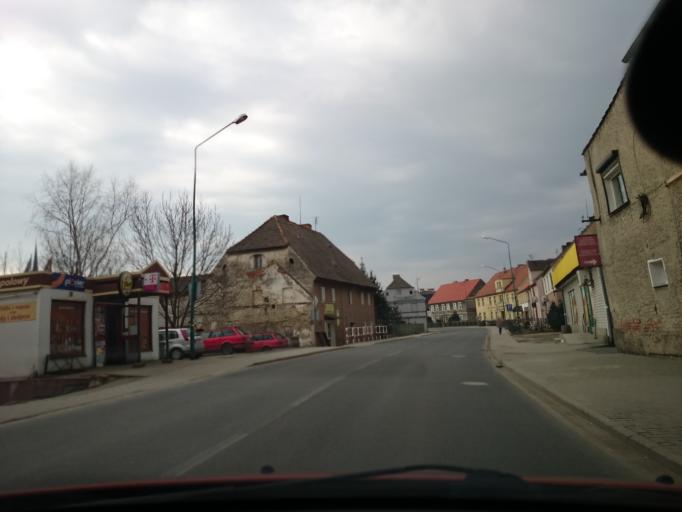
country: PL
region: Lower Silesian Voivodeship
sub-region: Powiat zabkowicki
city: Kamieniec Zabkowicki
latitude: 50.5226
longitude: 16.8732
